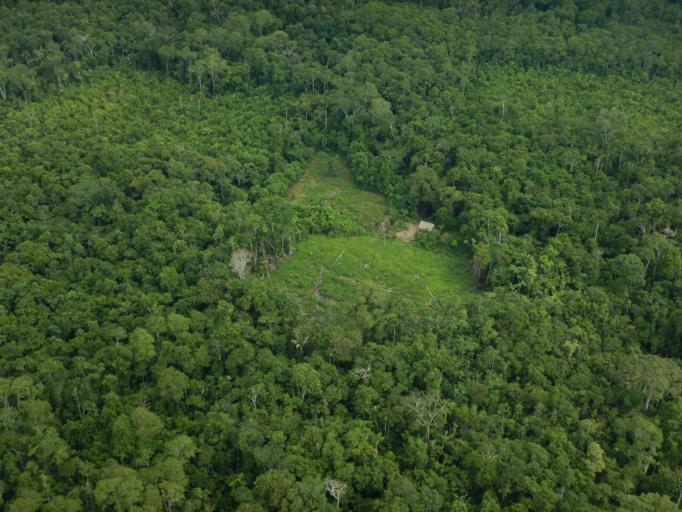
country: BO
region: Cochabamba
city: Chimore
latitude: -16.8929
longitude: -64.8582
